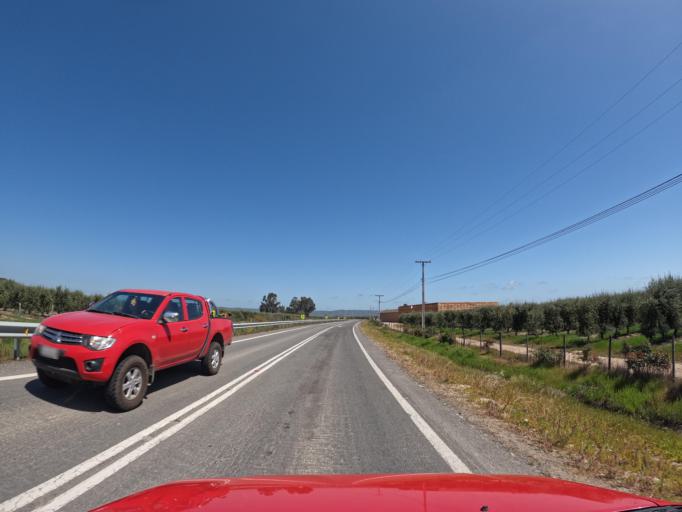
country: CL
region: O'Higgins
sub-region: Provincia de Colchagua
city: Santa Cruz
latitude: -34.7359
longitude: -71.7037
